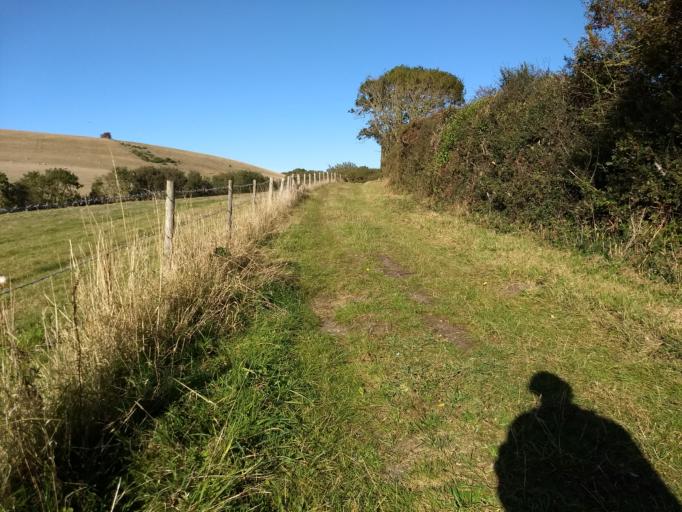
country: GB
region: England
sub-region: Isle of Wight
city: Newport
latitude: 50.6510
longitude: -1.2879
